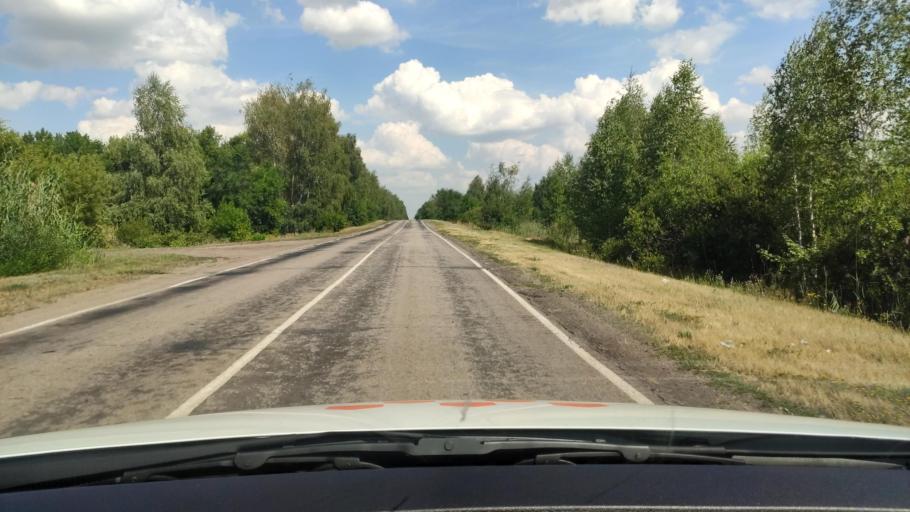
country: RU
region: Voronezj
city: Ertil'
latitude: 51.7839
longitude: 40.5684
